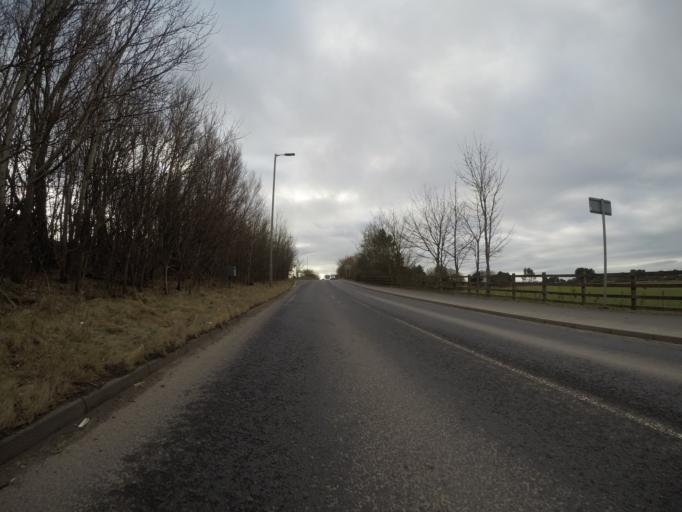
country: GB
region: Scotland
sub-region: South Ayrshire
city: Troon
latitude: 55.5703
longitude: -4.6394
